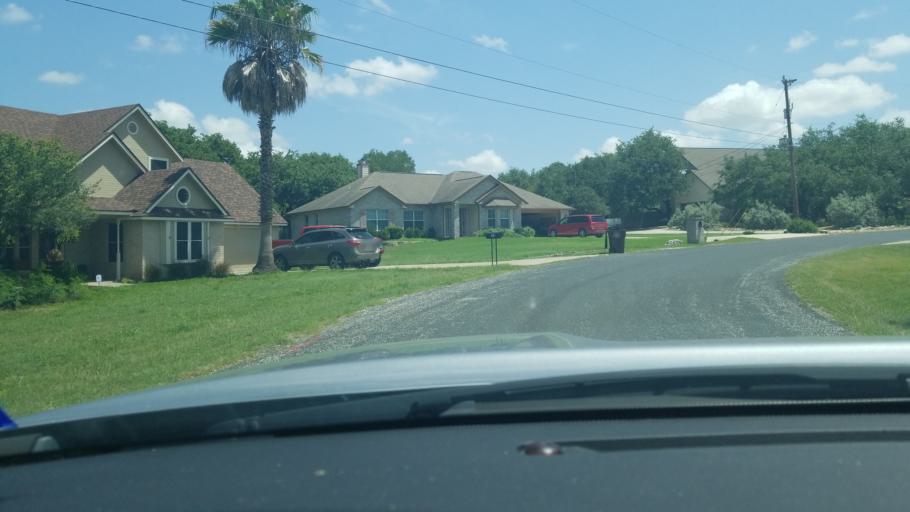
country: US
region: Texas
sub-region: Bexar County
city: Timberwood Park
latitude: 29.6881
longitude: -98.4874
